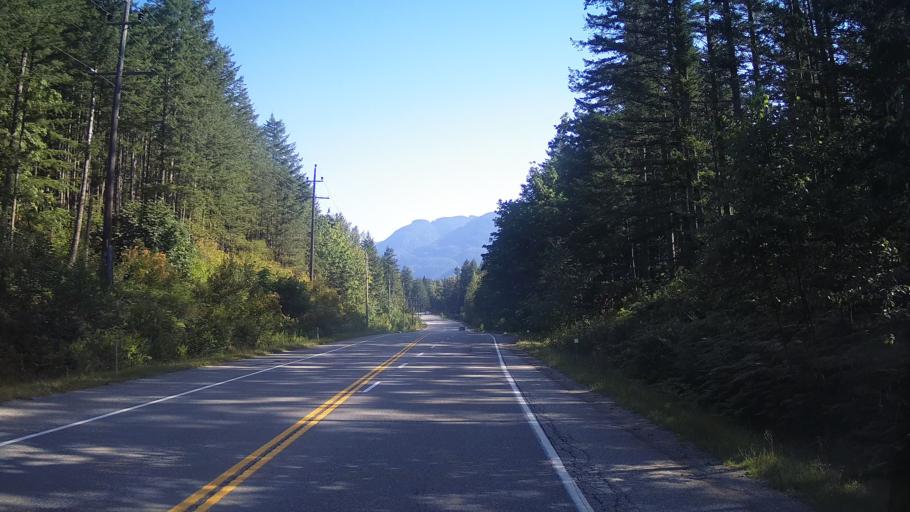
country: CA
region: British Columbia
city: Hope
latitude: 49.4354
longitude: -121.4390
